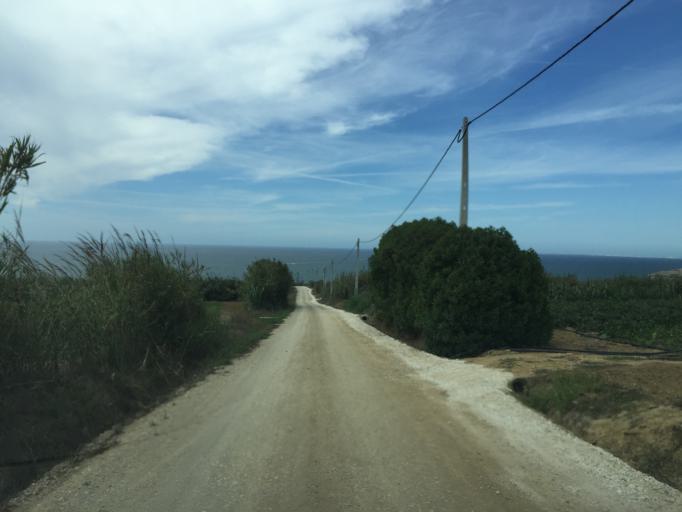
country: PT
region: Lisbon
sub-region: Lourinha
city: Lourinha
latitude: 39.1966
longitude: -9.3435
